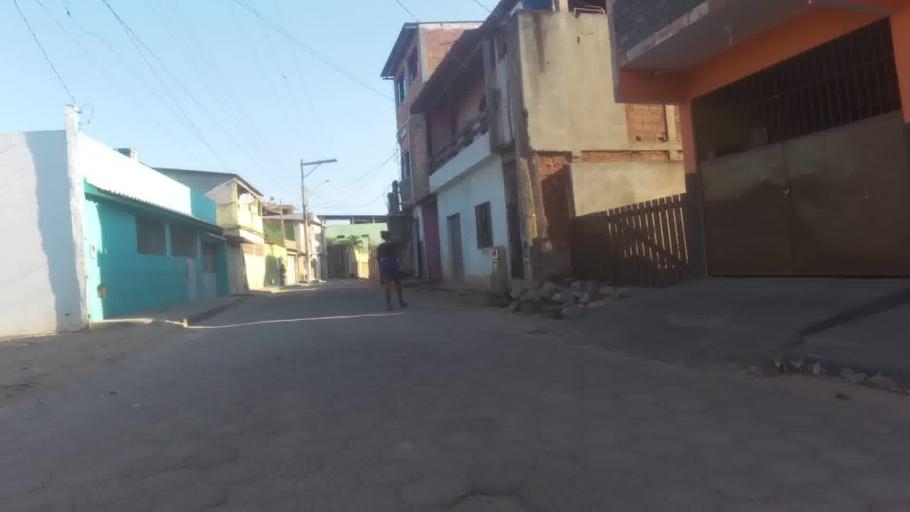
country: BR
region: Espirito Santo
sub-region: Itapemirim
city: Itapemirim
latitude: -21.0164
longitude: -40.8141
